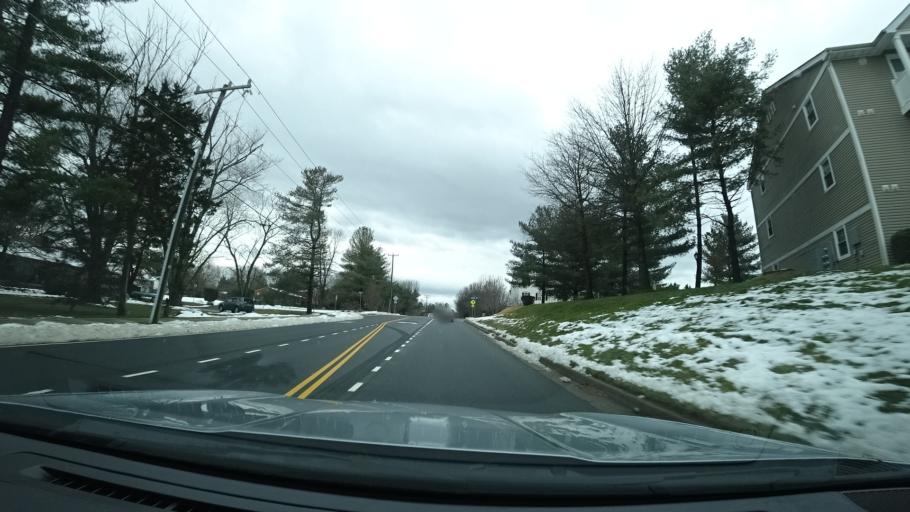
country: US
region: Virginia
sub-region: Loudoun County
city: Sugarland Run
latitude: 39.0076
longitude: -77.3791
